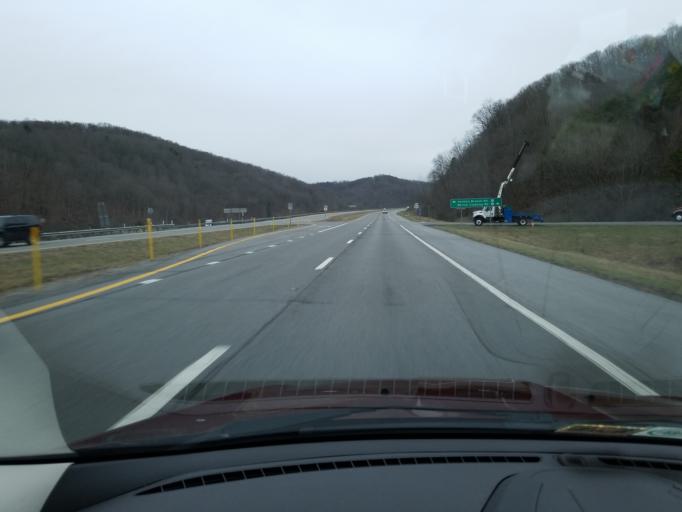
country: US
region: West Virginia
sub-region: Mercer County
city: Athens
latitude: 37.3418
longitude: -80.9991
